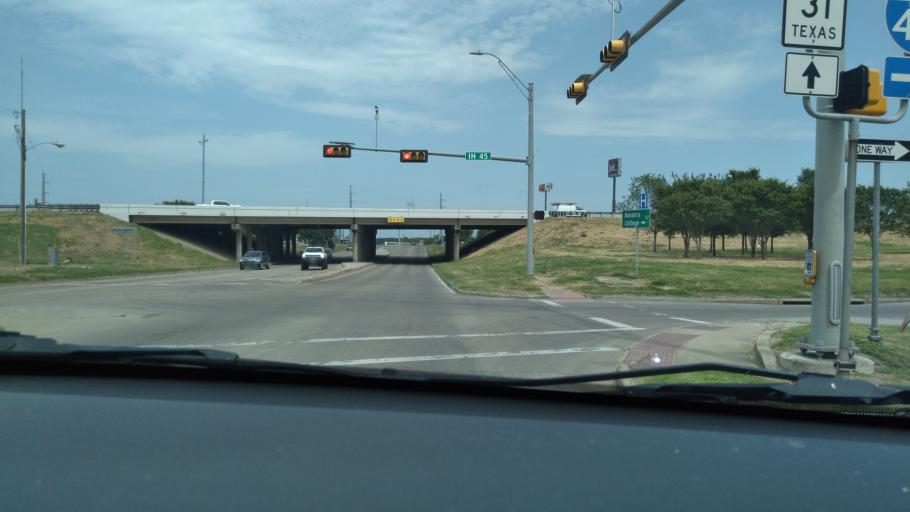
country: US
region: Texas
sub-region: Navarro County
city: Corsicana
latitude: 32.0984
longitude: -96.4422
